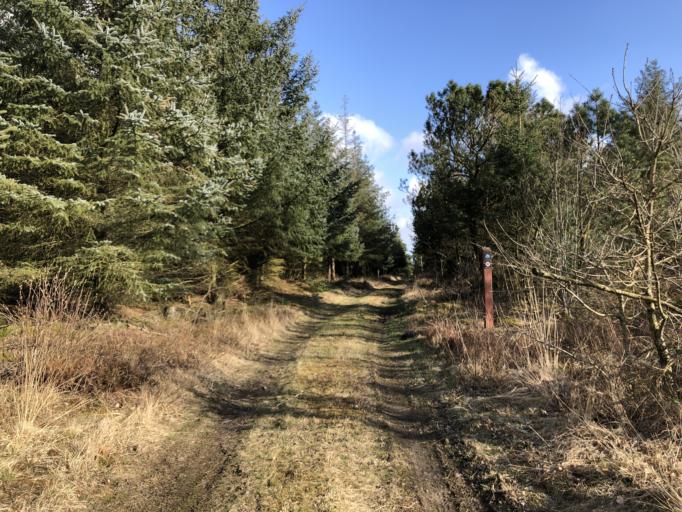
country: DK
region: Central Jutland
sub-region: Holstebro Kommune
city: Ulfborg
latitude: 56.2752
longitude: 8.3492
